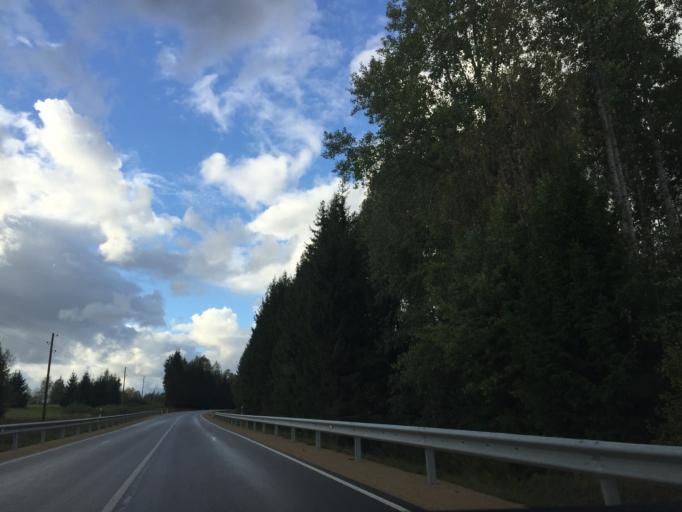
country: LV
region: Ligatne
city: Ligatne
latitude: 57.1637
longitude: 25.0519
